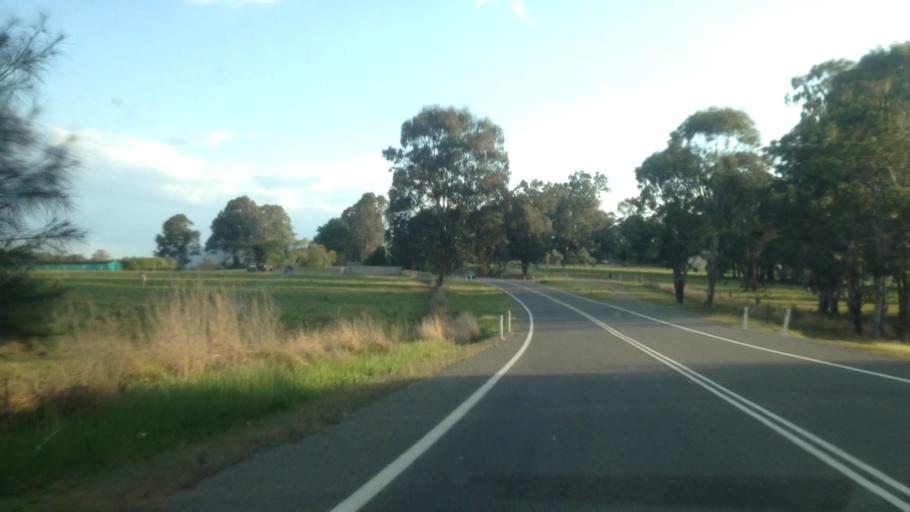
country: AU
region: New South Wales
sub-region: Cessnock
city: Kurri Kurri
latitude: -32.8640
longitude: 151.4809
